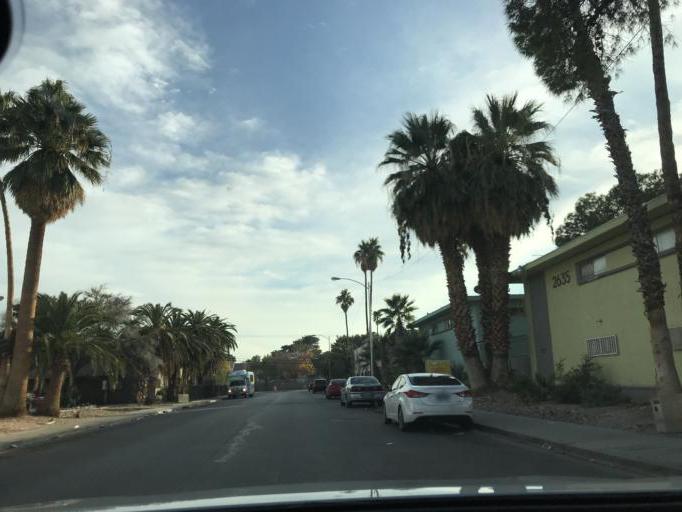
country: US
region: Nevada
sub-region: Clark County
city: Winchester
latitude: 36.1416
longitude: -115.1472
